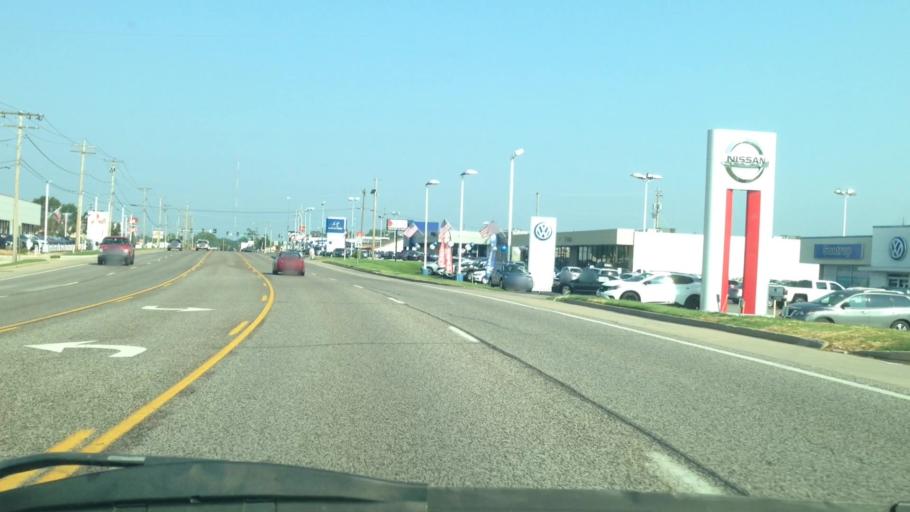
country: US
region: Missouri
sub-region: Saint Louis County
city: Green Park
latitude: 38.5202
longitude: -90.3440
